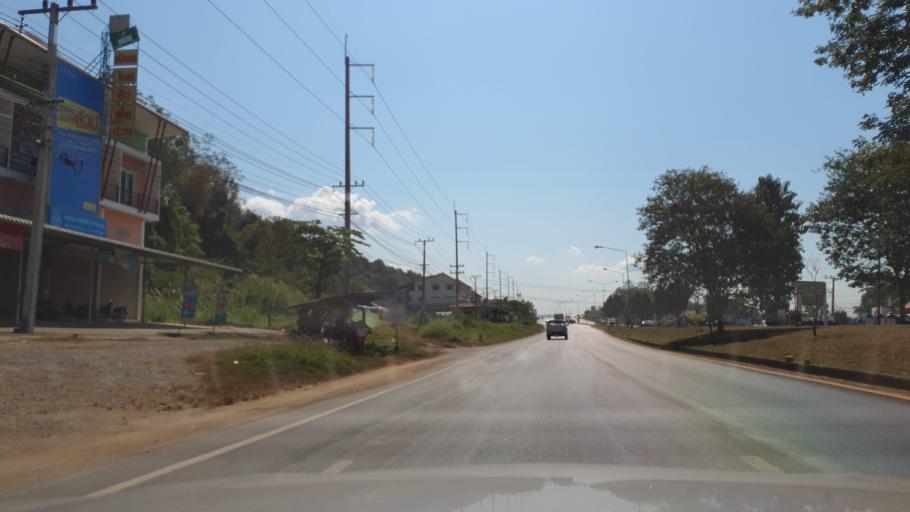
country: TH
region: Nan
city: Tha Wang Pha
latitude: 19.1019
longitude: 100.8086
